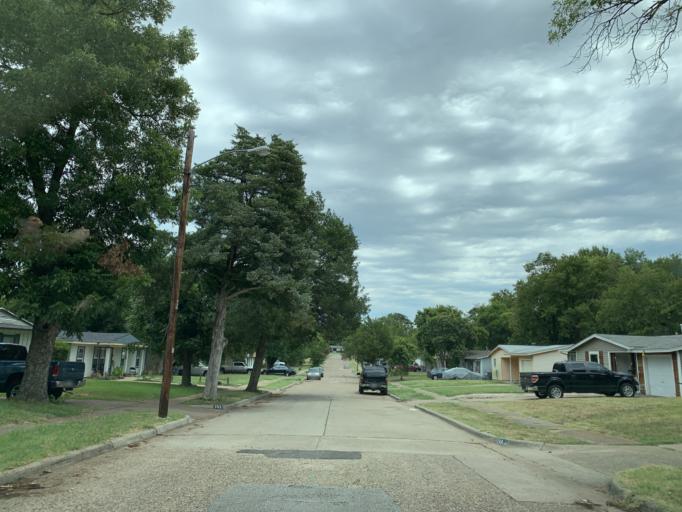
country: US
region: Texas
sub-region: Dallas County
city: DeSoto
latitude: 32.6599
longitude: -96.8347
